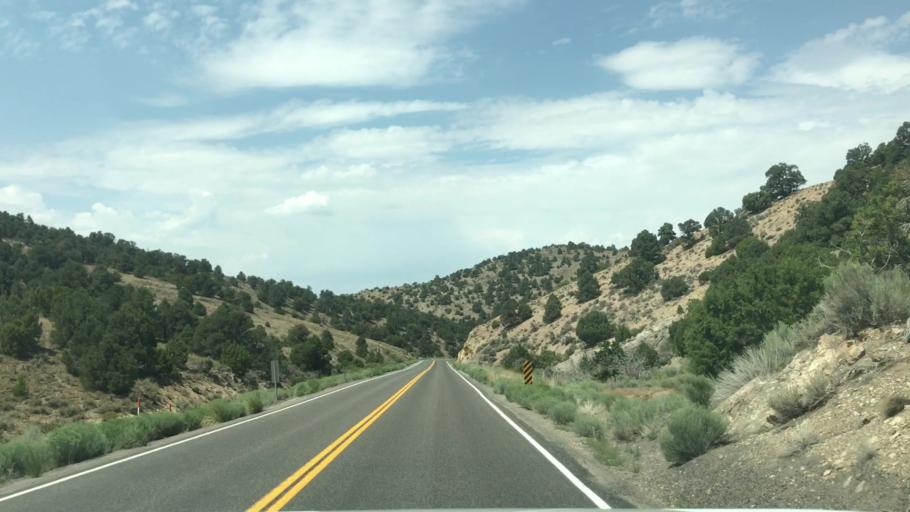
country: US
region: Nevada
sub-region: Eureka County
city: Eureka
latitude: 39.3951
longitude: -115.4809
